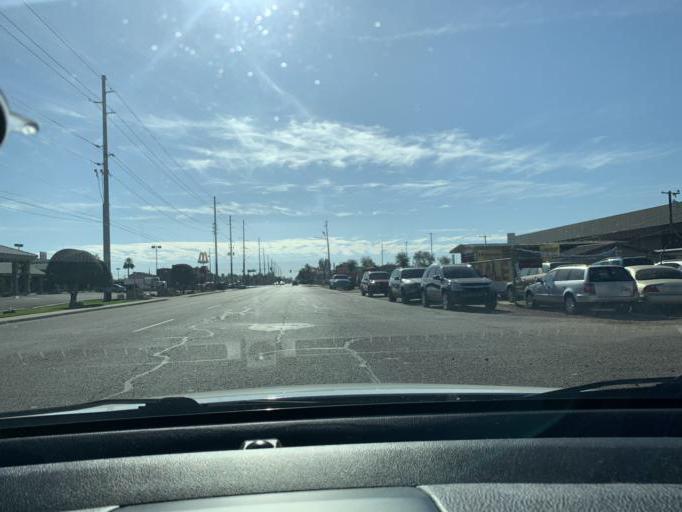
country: US
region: Arizona
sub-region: Maricopa County
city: Peoria
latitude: 33.6860
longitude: -112.1090
